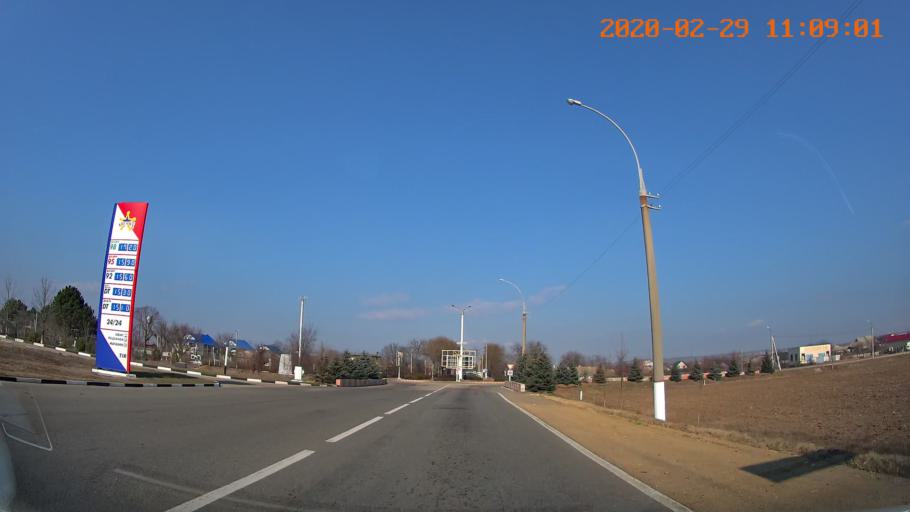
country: MD
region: Telenesti
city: Dubasari
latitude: 47.2388
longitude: 29.1718
